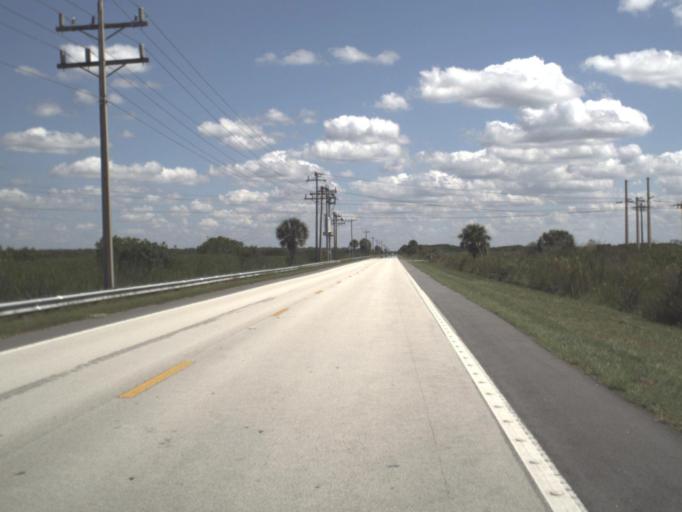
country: US
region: Florida
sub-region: Collier County
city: Marco
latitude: 25.9094
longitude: -81.3607
